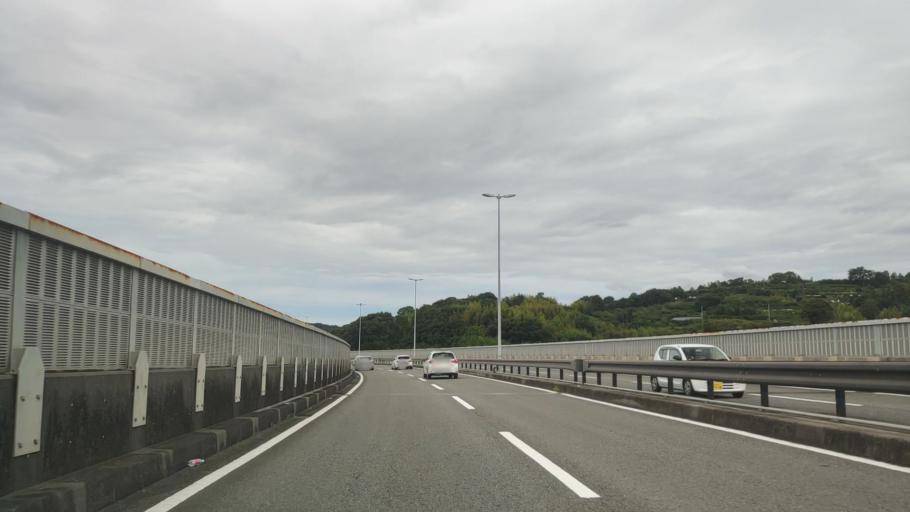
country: JP
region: Wakayama
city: Tanabe
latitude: 33.7431
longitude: 135.3861
